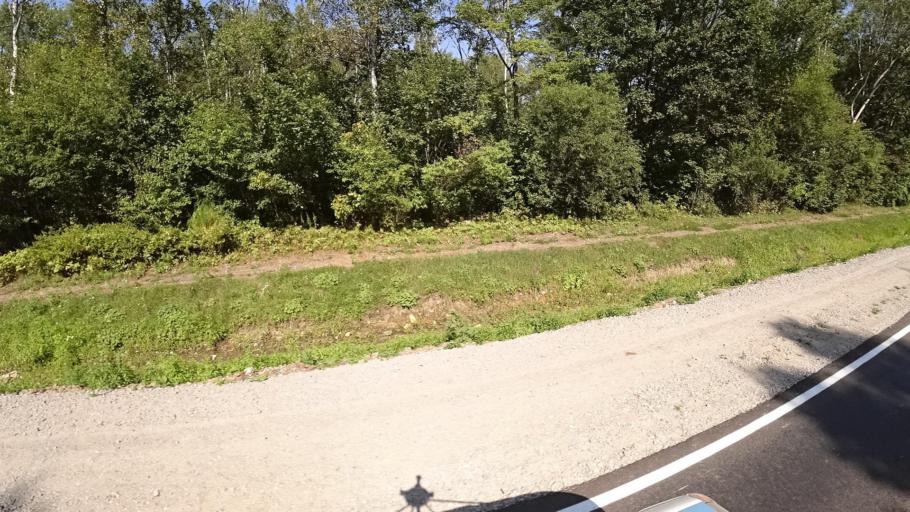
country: RU
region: Khabarovsk Krai
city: Khor
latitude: 47.9762
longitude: 135.0774
